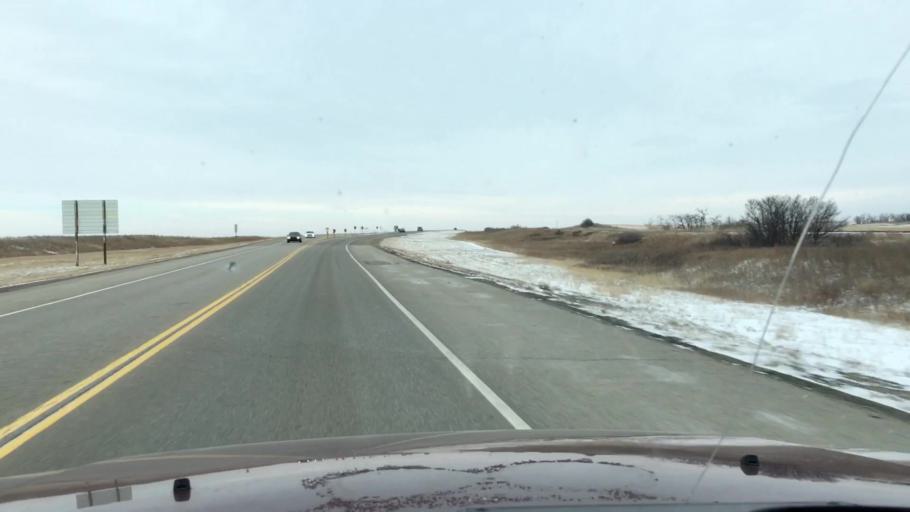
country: CA
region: Saskatchewan
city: Moose Jaw
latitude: 50.8445
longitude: -105.5544
